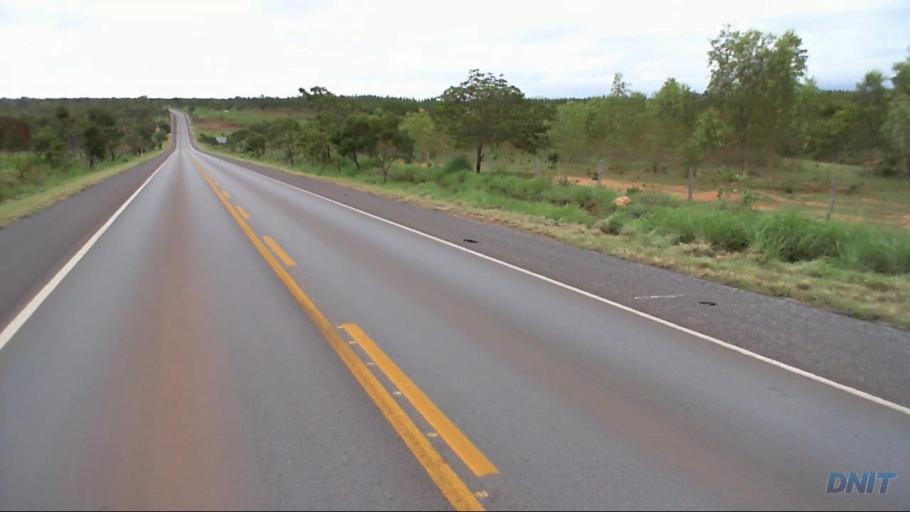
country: BR
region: Goias
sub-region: Barro Alto
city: Barro Alto
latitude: -15.2126
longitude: -48.6639
